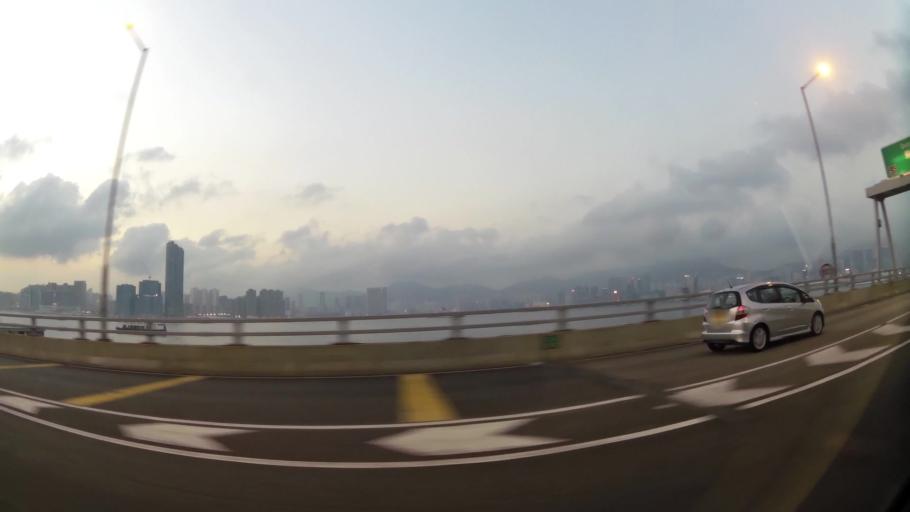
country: HK
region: Kowloon City
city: Kowloon
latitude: 22.2942
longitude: 114.2025
